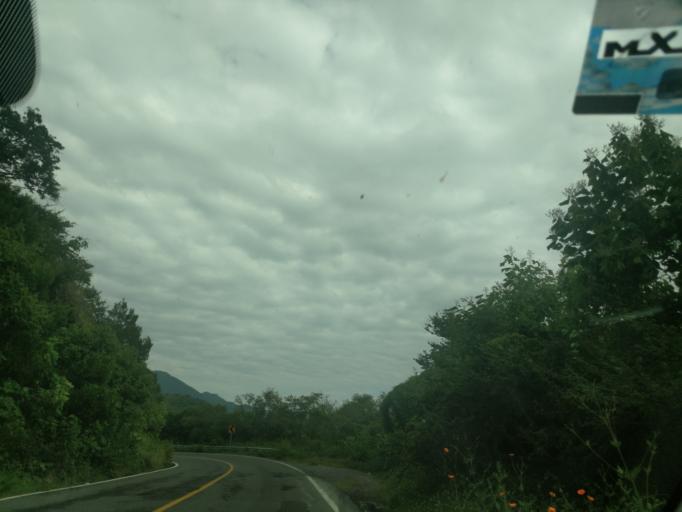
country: MX
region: Jalisco
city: Ameca
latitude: 20.5290
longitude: -104.2329
